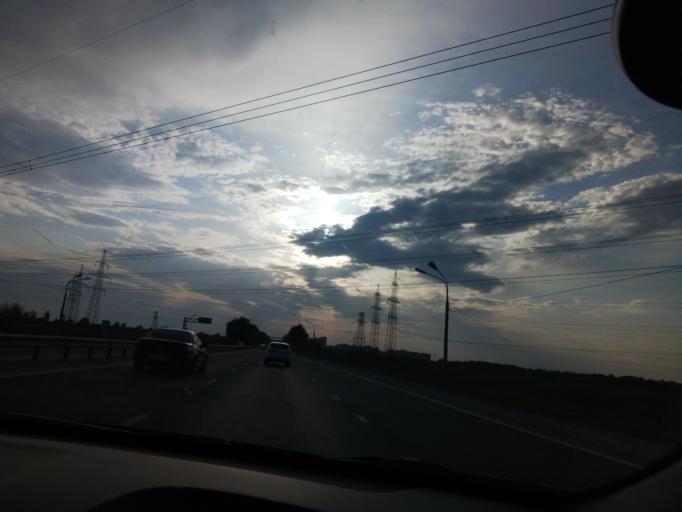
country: RU
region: Chuvashia
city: Novocheboksarsk
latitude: 56.1226
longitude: 47.4187
